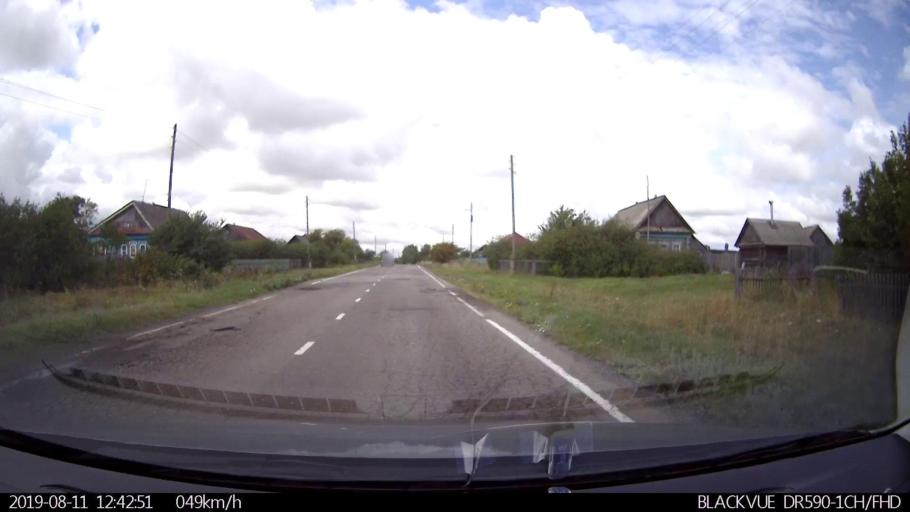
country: RU
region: Ulyanovsk
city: Ignatovka
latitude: 53.8486
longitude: 47.7470
